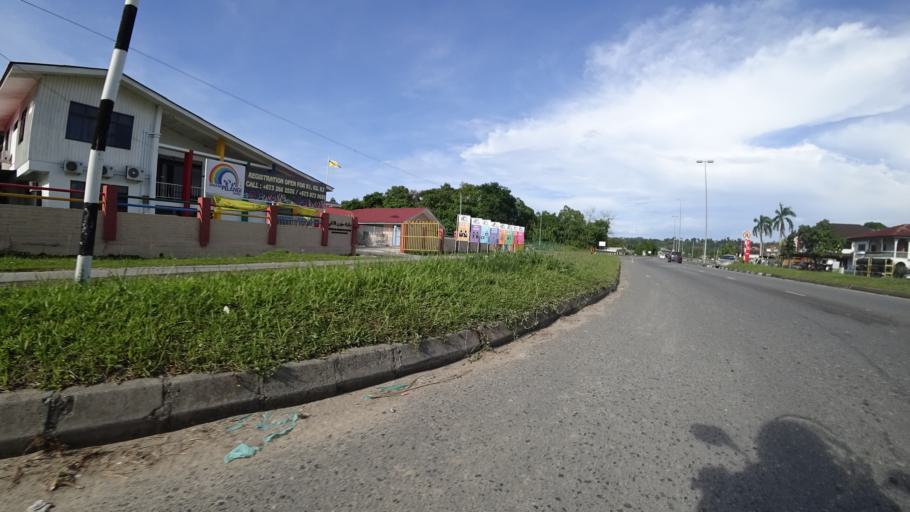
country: BN
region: Brunei and Muara
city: Bandar Seri Begawan
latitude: 4.8933
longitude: 114.8475
